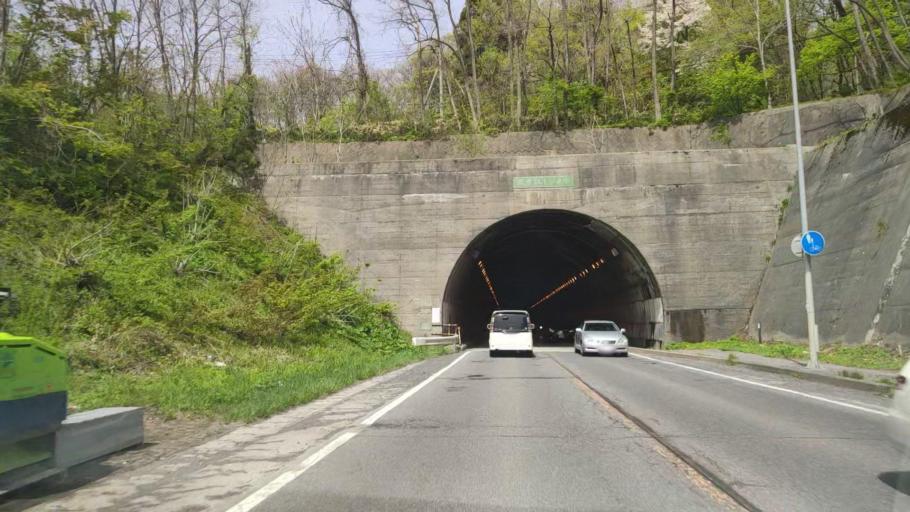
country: JP
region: Aomori
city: Aomori Shi
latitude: 40.8558
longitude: 140.8401
